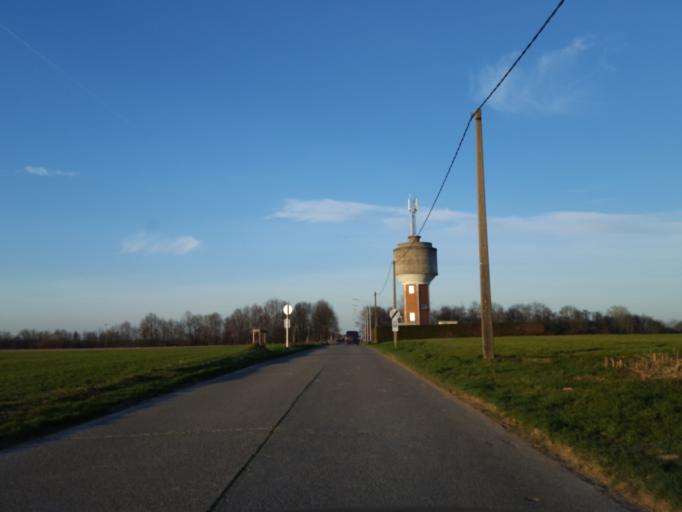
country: BE
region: Wallonia
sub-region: Province du Brabant Wallon
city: Walhain-Saint-Paul
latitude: 50.6545
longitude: 4.6675
